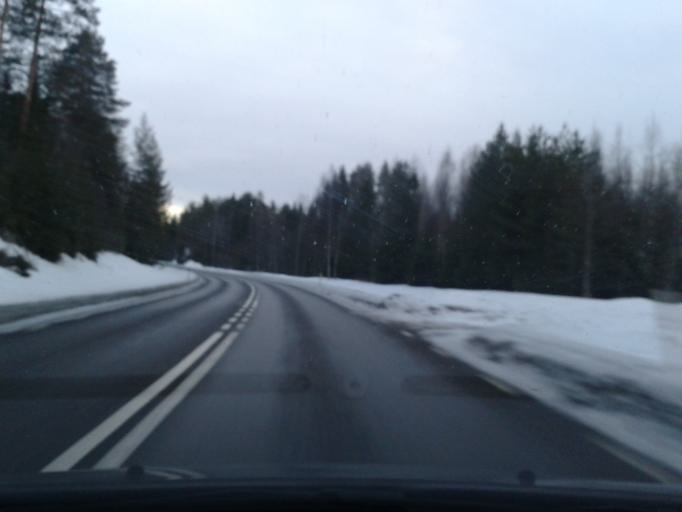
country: SE
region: Vaesternorrland
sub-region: Kramfors Kommun
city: Bollstabruk
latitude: 63.1013
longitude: 17.5127
